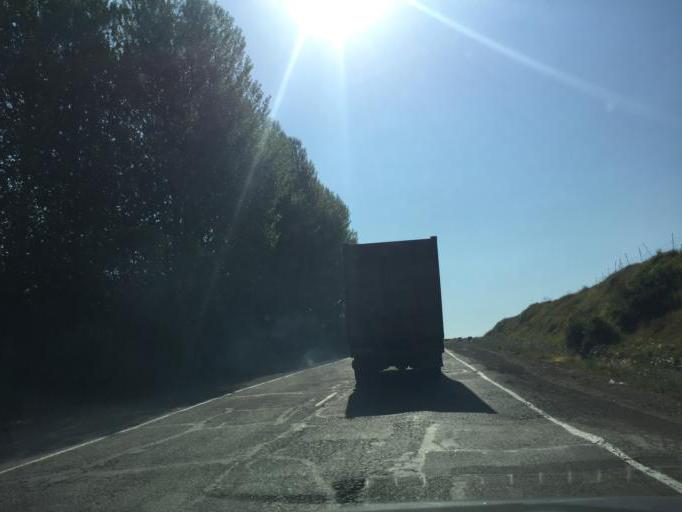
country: AM
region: Ararat
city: Zangakatun
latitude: 39.8136
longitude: 45.0487
